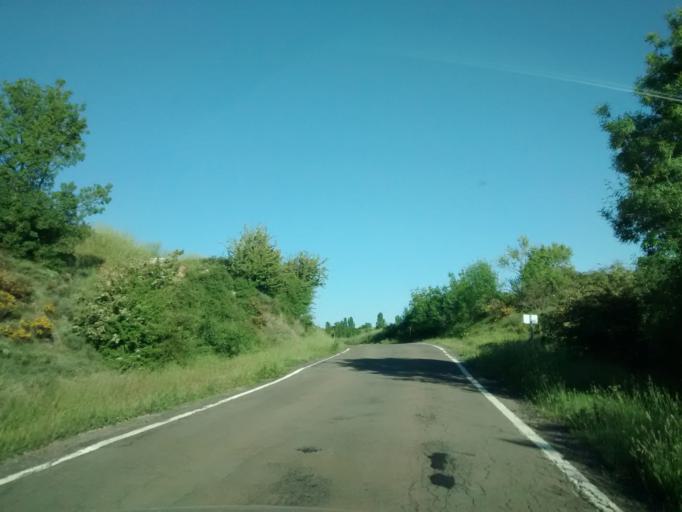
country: ES
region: Aragon
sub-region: Provincia de Huesca
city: Jaca
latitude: 42.5943
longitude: -0.6135
